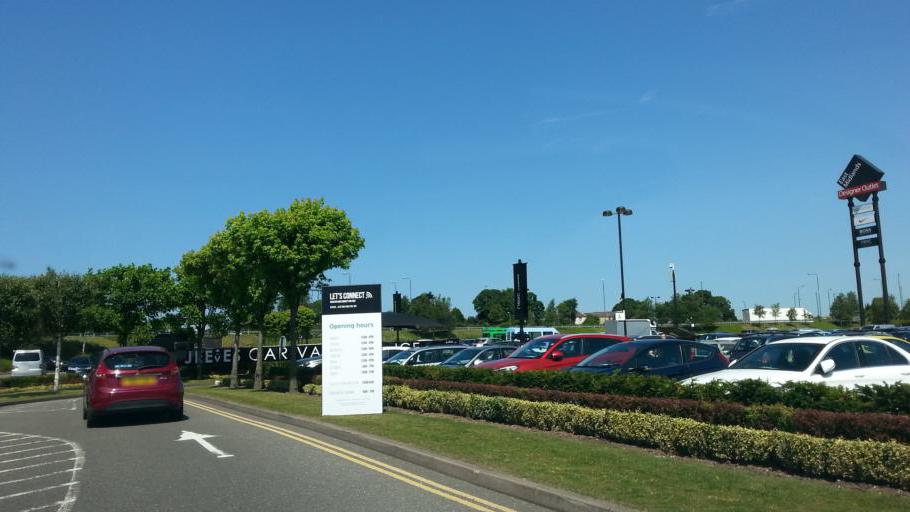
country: GB
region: England
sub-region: Derbyshire
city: Pinxton
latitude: 53.1072
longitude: -1.3129
